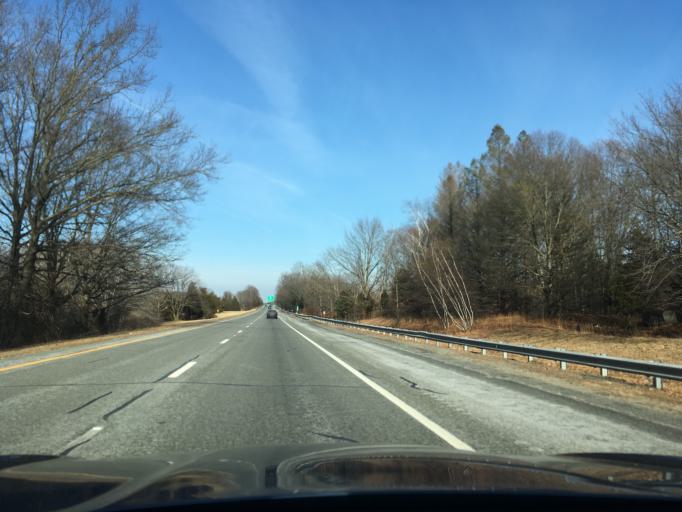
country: US
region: Rhode Island
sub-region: Kent County
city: West Warwick
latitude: 41.7416
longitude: -71.4881
